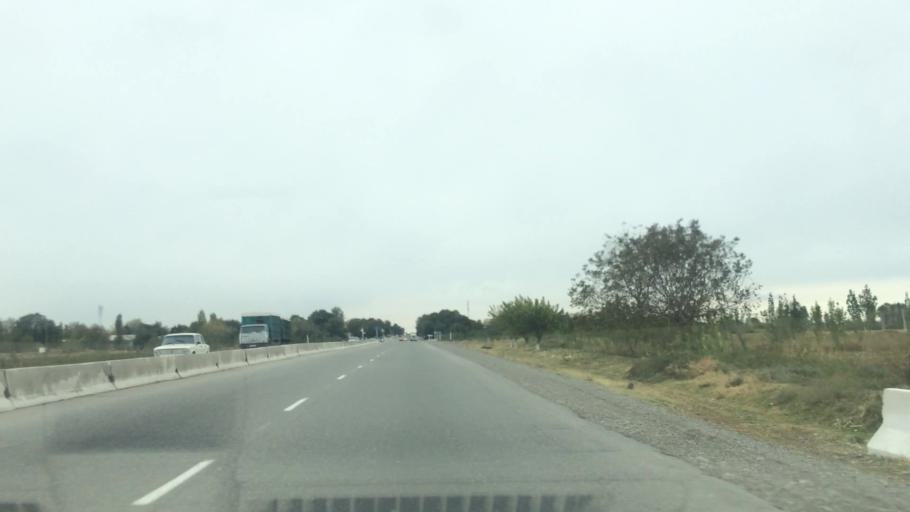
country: UZ
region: Samarqand
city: Bulung'ur
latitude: 39.7400
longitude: 67.1904
